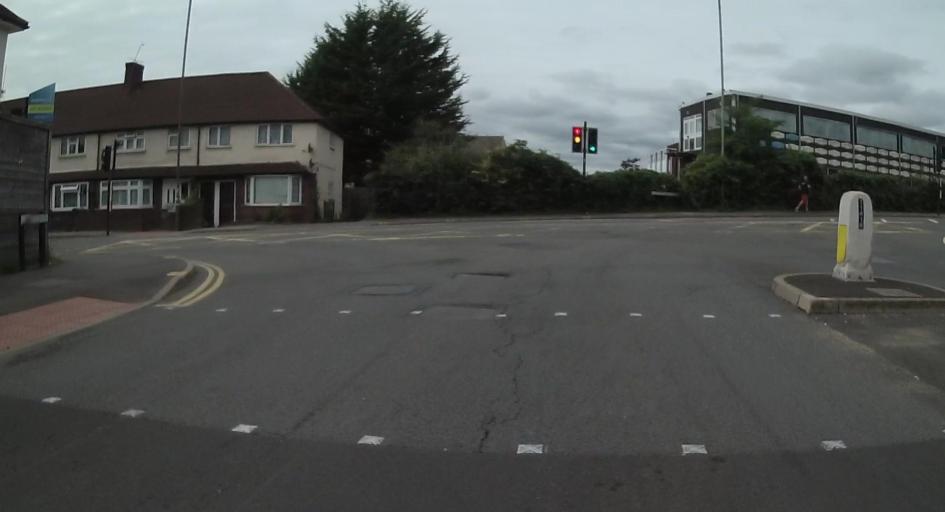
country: GB
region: England
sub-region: Surrey
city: Woking
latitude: 51.3271
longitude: -0.5425
